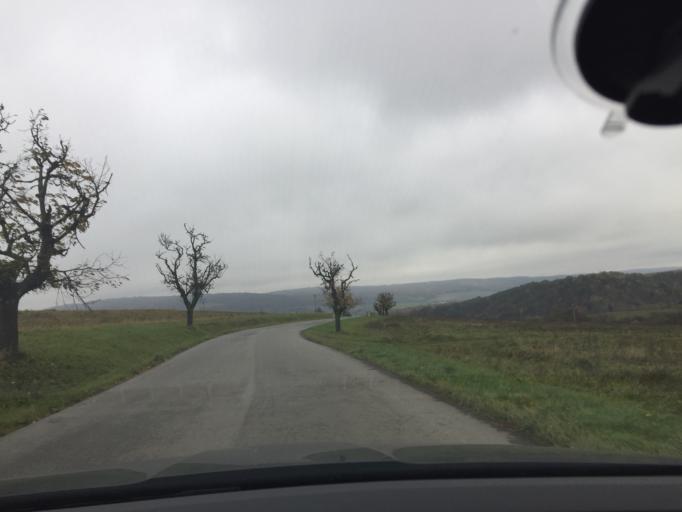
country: SK
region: Presovsky
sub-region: Okres Bardejov
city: Bardejov
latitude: 49.2508
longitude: 21.2163
